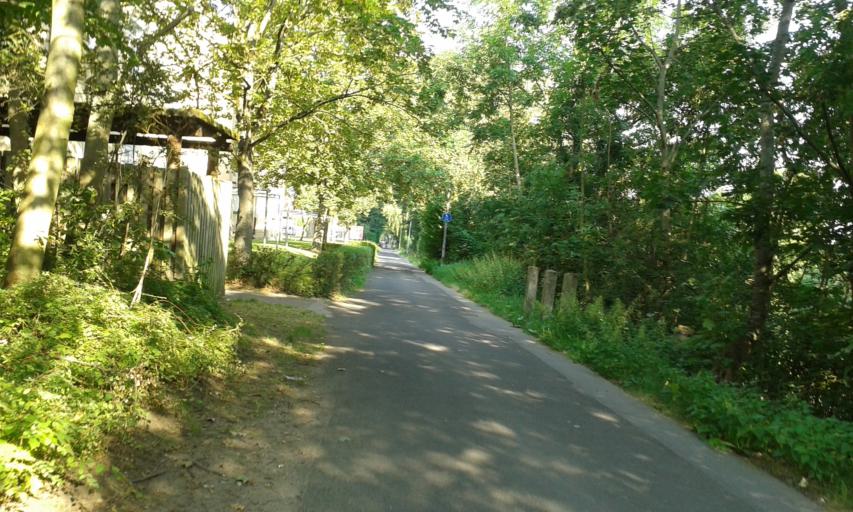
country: DE
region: Bavaria
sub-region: Upper Franconia
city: Hallstadt
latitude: 49.9030
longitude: 10.8664
